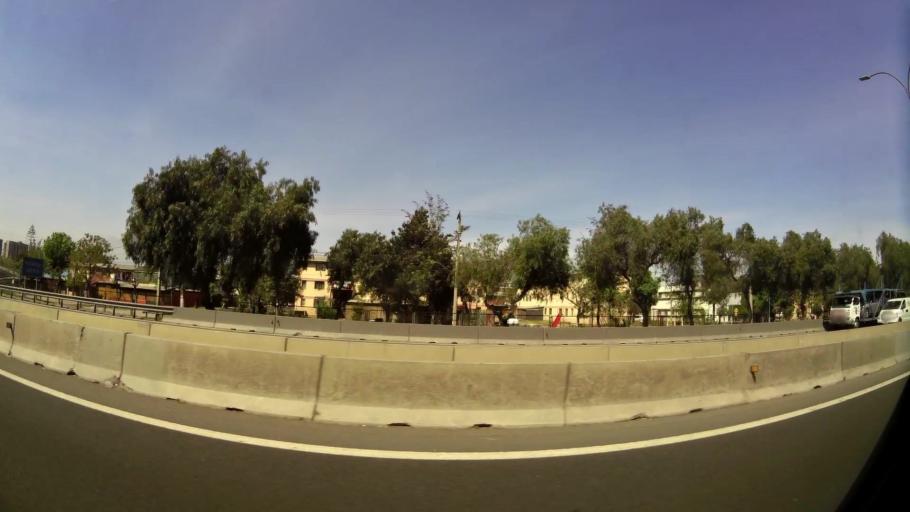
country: CL
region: Santiago Metropolitan
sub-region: Provincia de Santiago
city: Santiago
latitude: -33.5158
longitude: -70.6735
